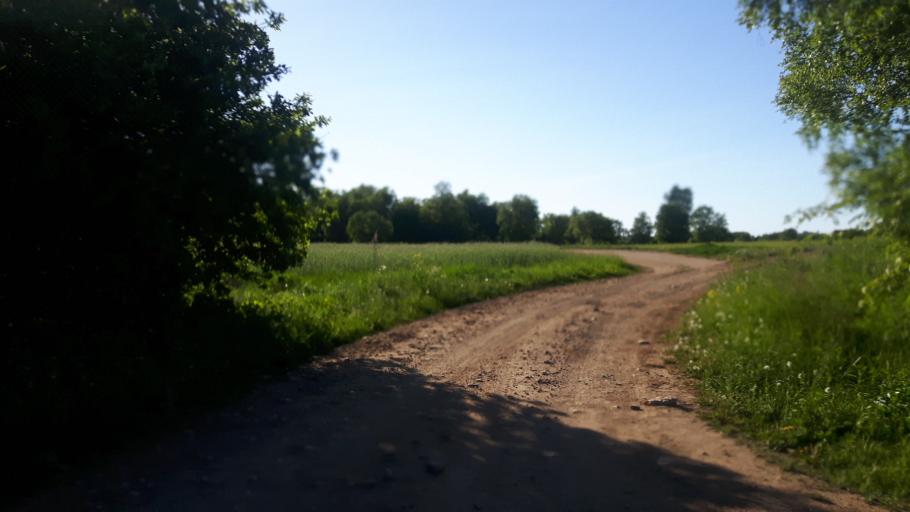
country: EE
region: Ida-Virumaa
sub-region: Puessi linn
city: Pussi
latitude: 59.4208
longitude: 27.0626
